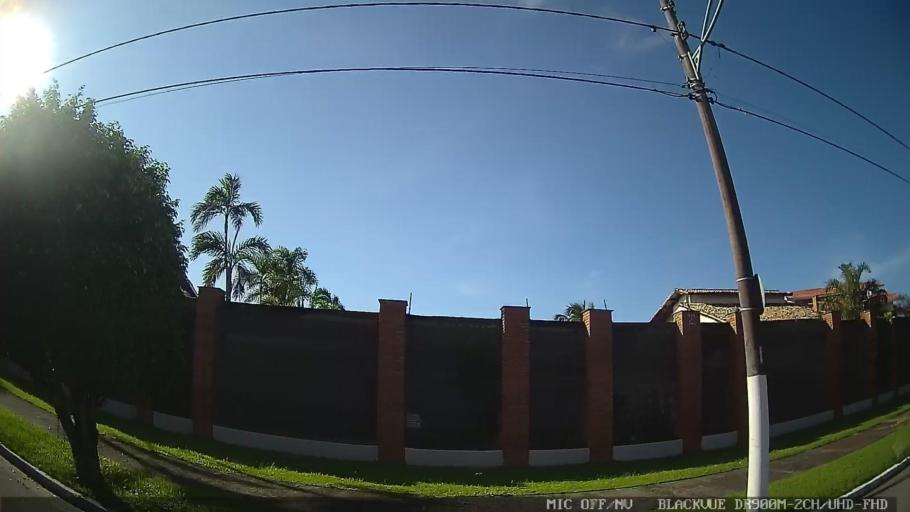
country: BR
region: Sao Paulo
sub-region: Peruibe
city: Peruibe
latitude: -24.2831
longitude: -46.9526
